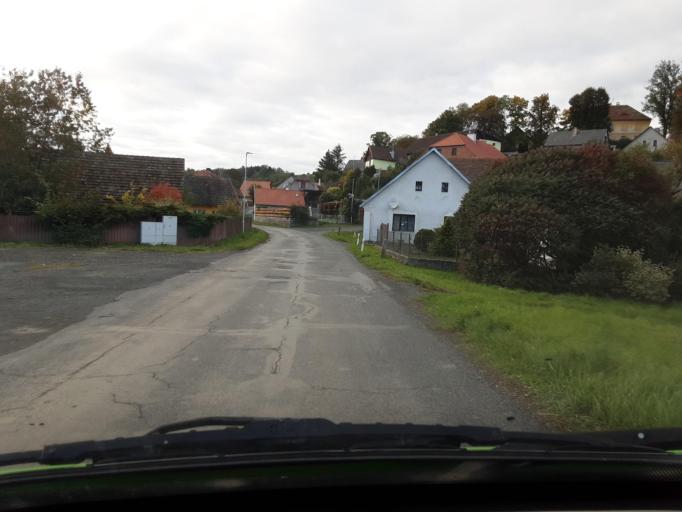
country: CZ
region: Plzensky
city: Janovice nad Uhlavou
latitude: 49.4243
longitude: 13.1784
